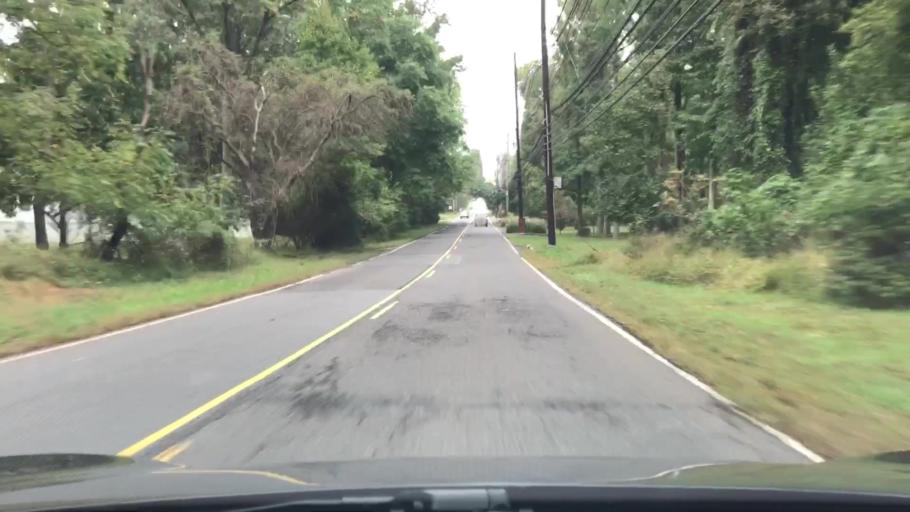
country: US
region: New Jersey
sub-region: Mercer County
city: Ewing
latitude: 40.2870
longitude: -74.7753
